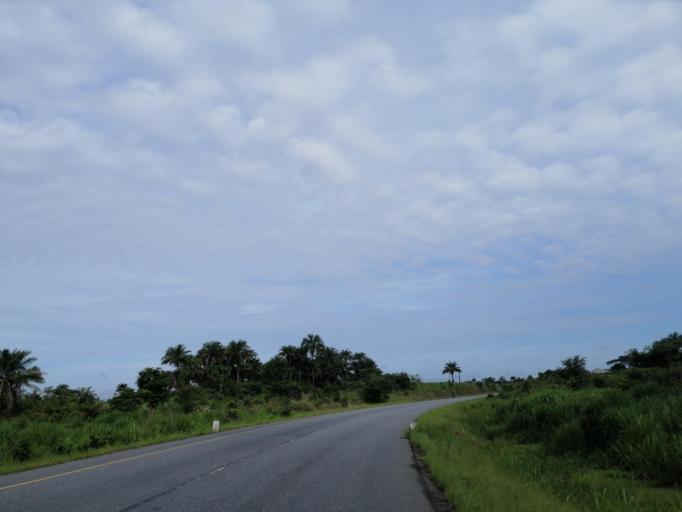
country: SL
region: Northern Province
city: Port Loko
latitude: 8.7721
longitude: -12.8614
